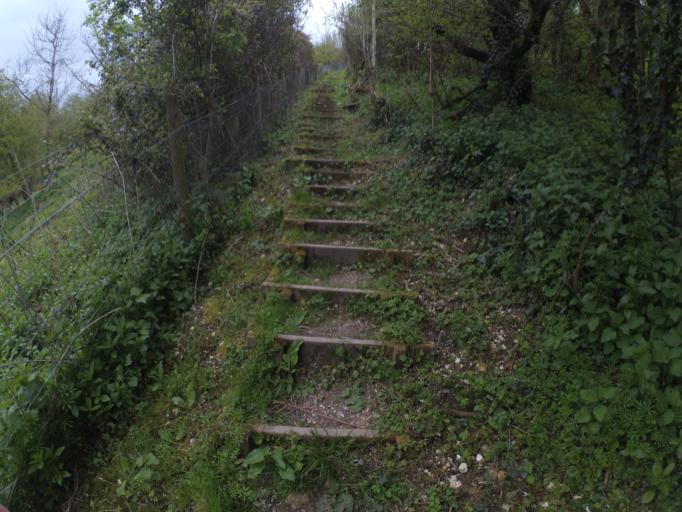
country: GB
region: England
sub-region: West Sussex
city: Arundel
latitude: 50.8828
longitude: -0.5237
